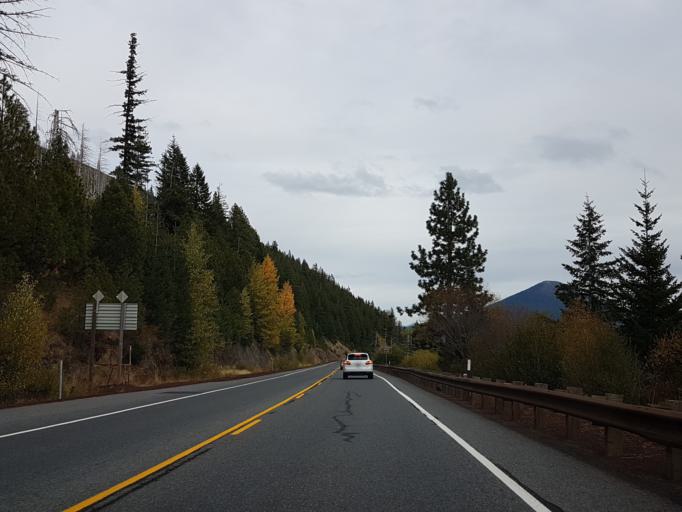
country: US
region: Oregon
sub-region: Deschutes County
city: Sisters
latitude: 44.4186
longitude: -121.7796
